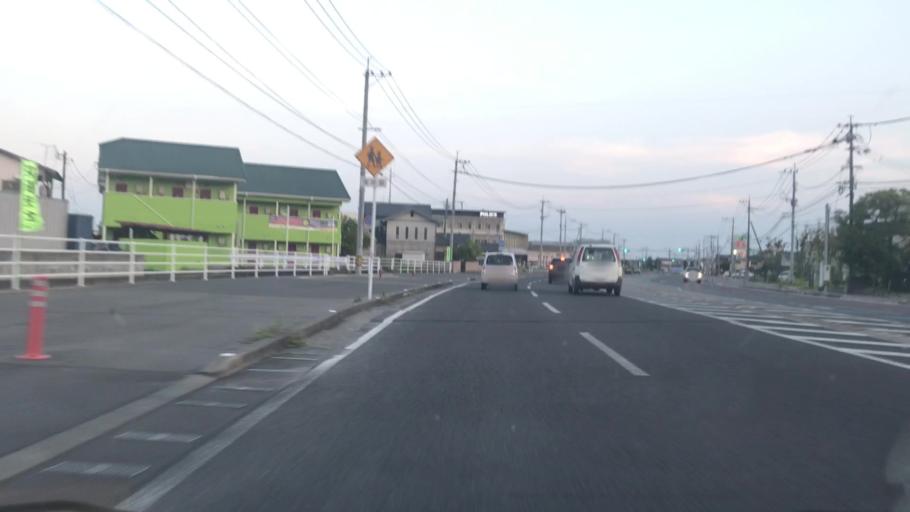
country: JP
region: Saga Prefecture
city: Saga-shi
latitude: 33.2386
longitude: 130.2945
